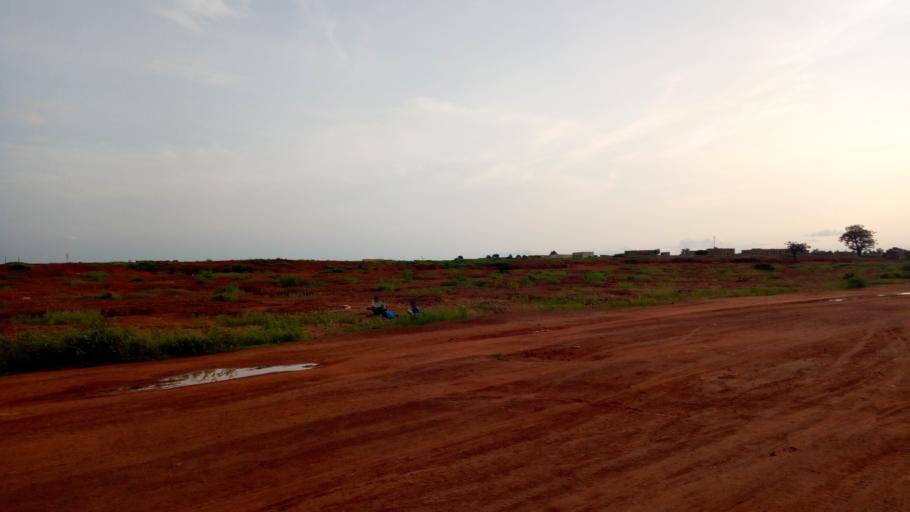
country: ML
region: Sikasso
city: Koutiala
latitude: 12.3748
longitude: -5.4977
